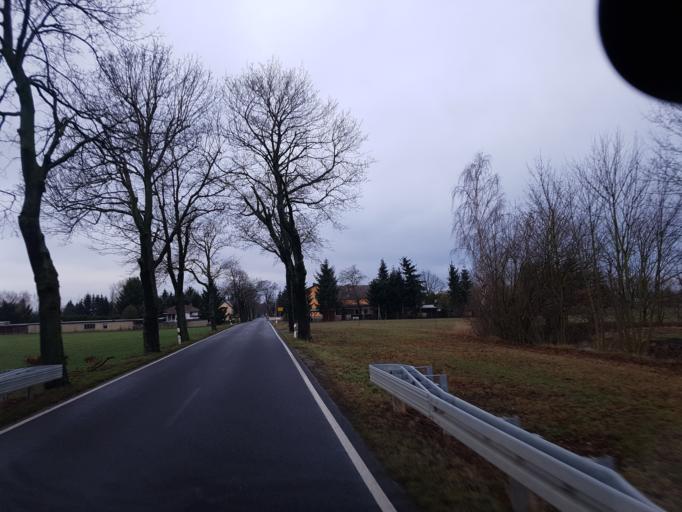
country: DE
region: Brandenburg
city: Plessa
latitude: 51.4340
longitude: 13.6251
